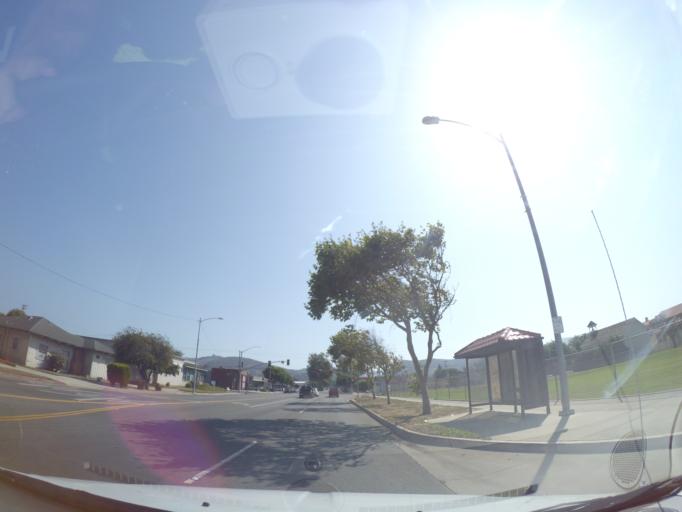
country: US
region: California
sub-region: Santa Barbara County
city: Lompoc
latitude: 34.6430
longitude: -120.4580
